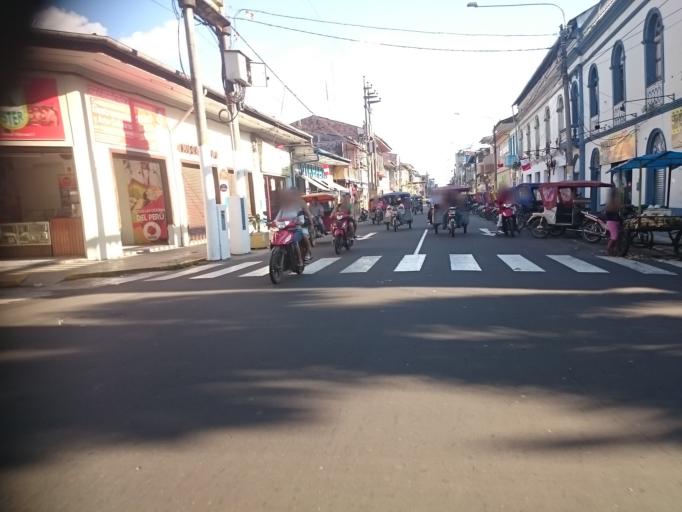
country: PE
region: Loreto
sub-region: Provincia de Maynas
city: Iquitos
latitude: -3.7528
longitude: -73.2461
